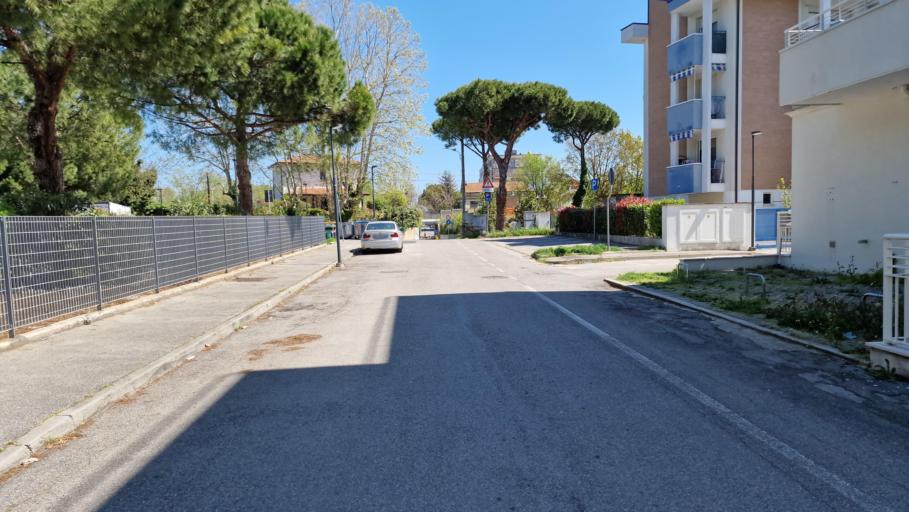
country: IT
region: Emilia-Romagna
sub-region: Provincia di Rimini
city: Bellaria-Igea Marina
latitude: 44.1396
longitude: 12.4696
